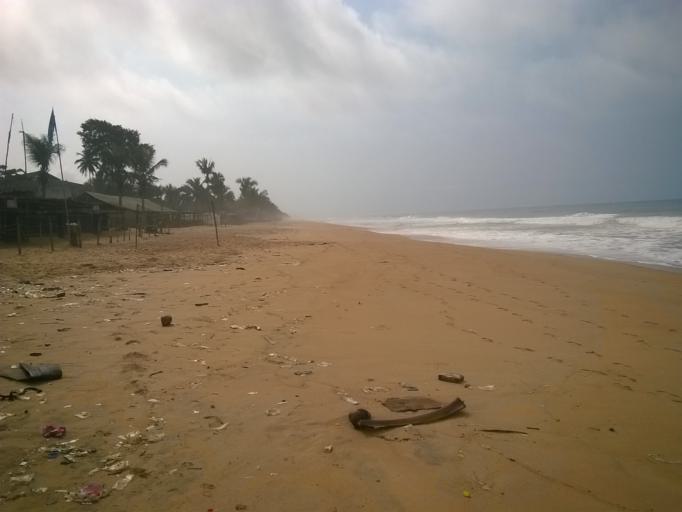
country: CI
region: Sud-Comoe
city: Grand-Bassam
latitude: 5.1946
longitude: -3.7393
